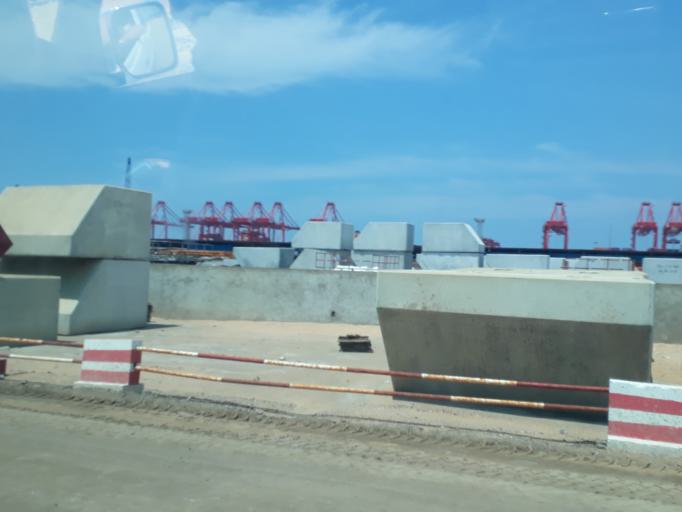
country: LK
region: Western
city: Colombo
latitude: 6.9383
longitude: 79.8367
